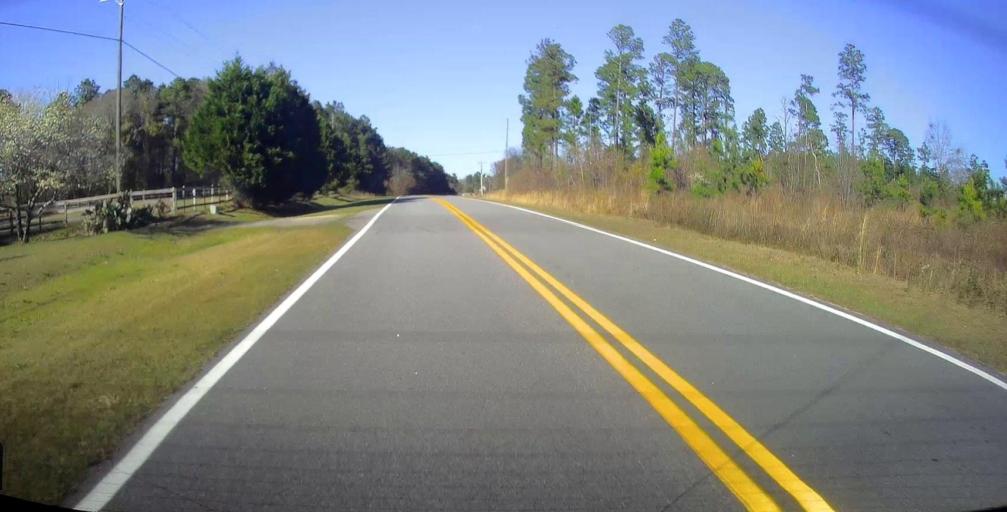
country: US
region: Georgia
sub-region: Peach County
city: Byron
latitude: 32.6799
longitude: -83.8083
